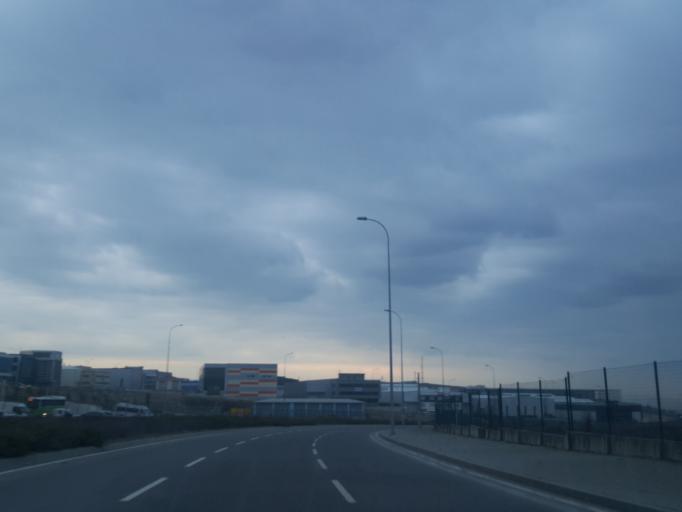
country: TR
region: Kocaeli
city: Tavsancil
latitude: 40.8295
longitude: 29.5692
